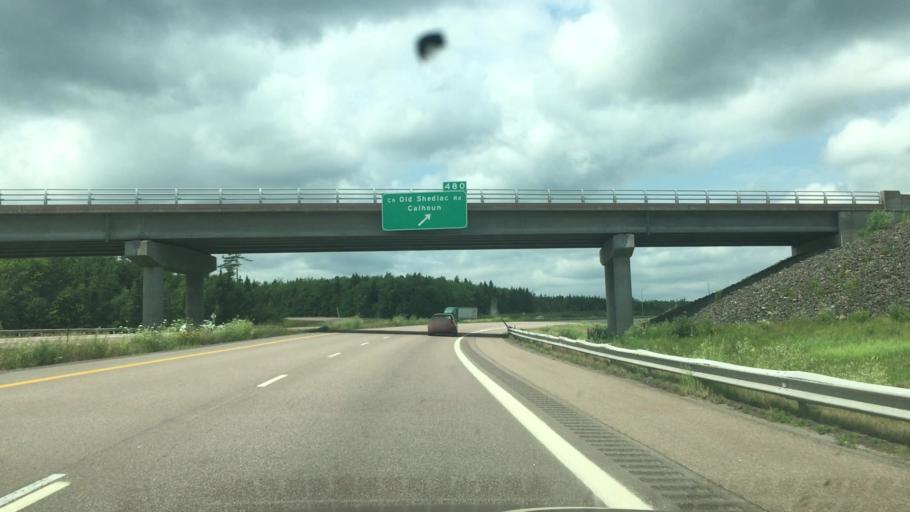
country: CA
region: New Brunswick
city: Dieppe
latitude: 46.0485
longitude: -64.5803
